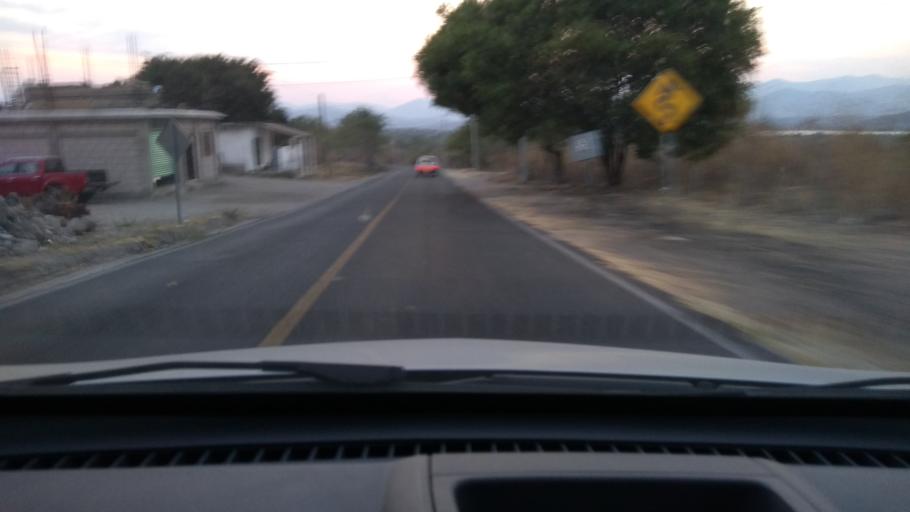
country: MX
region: Morelos
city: Coatetelco
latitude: 18.7218
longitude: -99.3058
